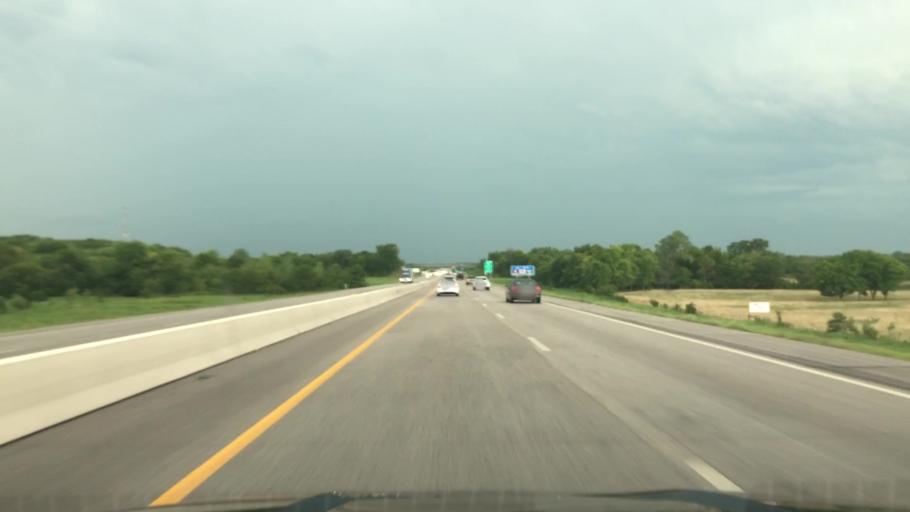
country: US
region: Oklahoma
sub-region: Rogers County
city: Justice
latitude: 36.3170
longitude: -95.5553
